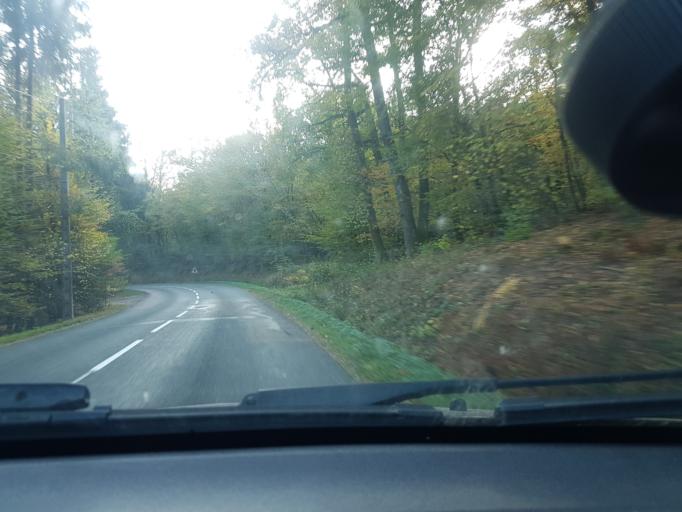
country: FR
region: Franche-Comte
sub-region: Departement de la Haute-Saone
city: Frahier-et-Chatebier
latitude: 47.6680
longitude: 6.7362
